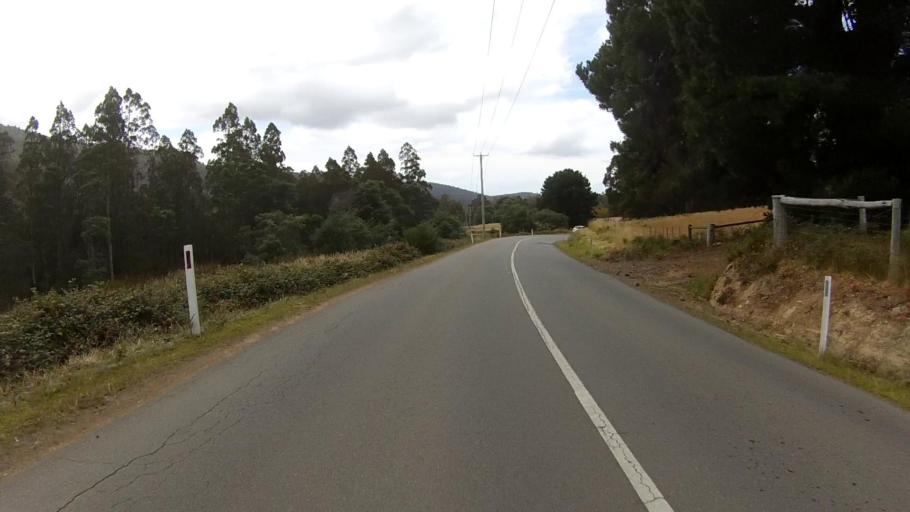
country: AU
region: Tasmania
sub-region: Kingborough
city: Kettering
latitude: -43.1124
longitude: 147.1950
